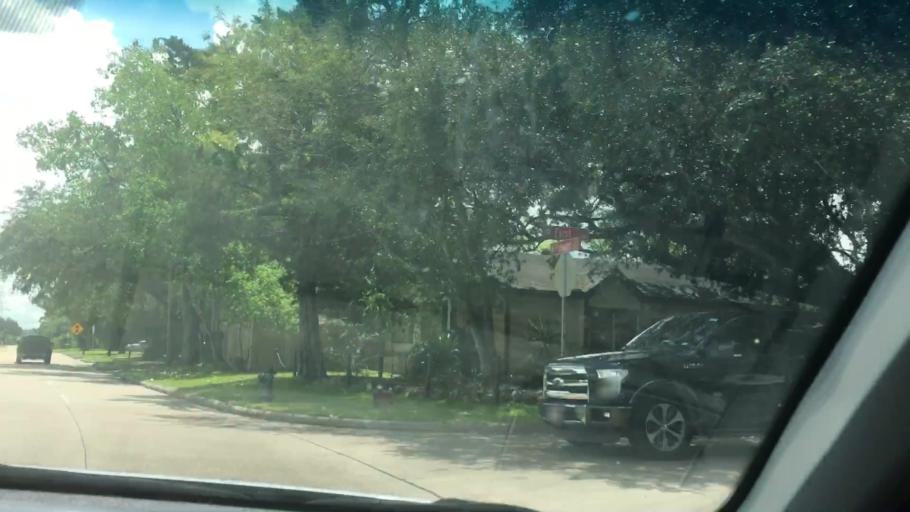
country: US
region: Texas
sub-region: Fort Bend County
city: Missouri City
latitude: 29.6129
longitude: -95.5460
